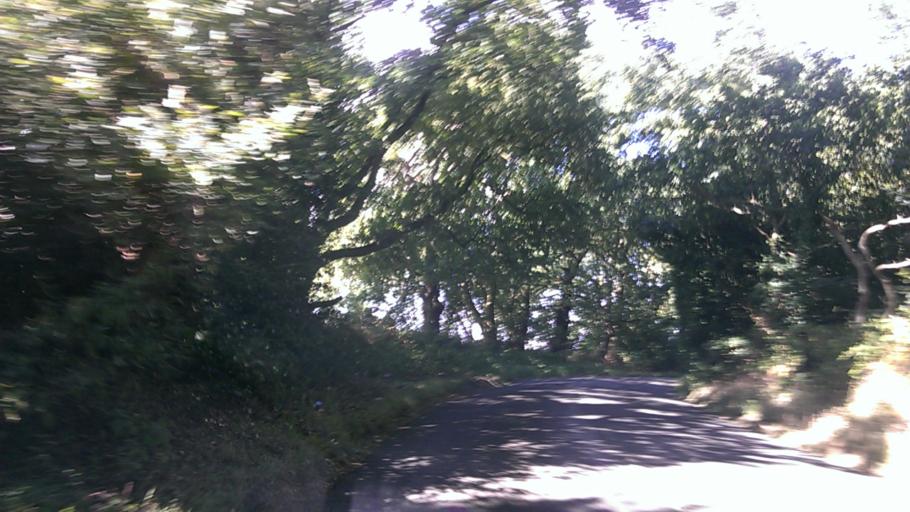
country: GB
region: England
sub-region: Essex
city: Layer de la Haye
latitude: 51.8502
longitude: 0.8815
